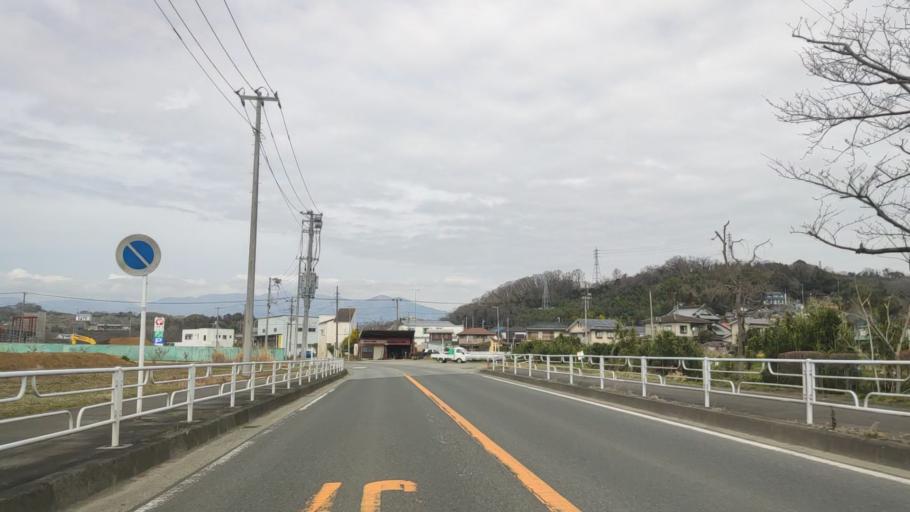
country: JP
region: Kanagawa
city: Ninomiya
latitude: 35.3159
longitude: 139.2242
